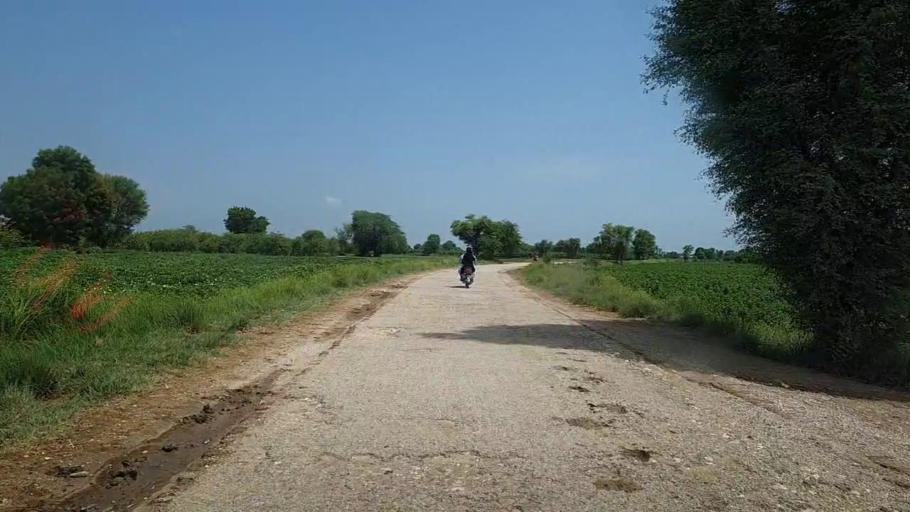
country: PK
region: Sindh
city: Bhiria
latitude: 26.8919
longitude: 68.1984
